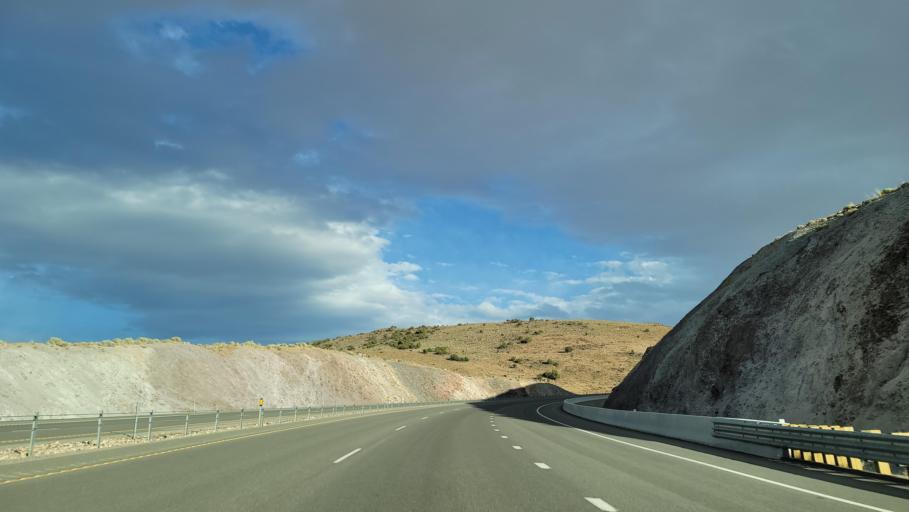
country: US
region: Nevada
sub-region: Lyon County
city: Stagecoach
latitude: 39.4892
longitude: -119.4021
